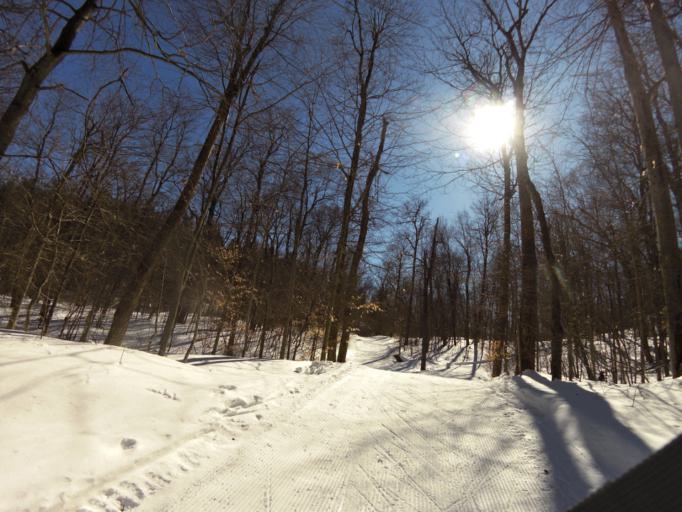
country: CA
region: Quebec
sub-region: Outaouais
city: Gatineau
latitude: 45.5046
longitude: -75.8615
